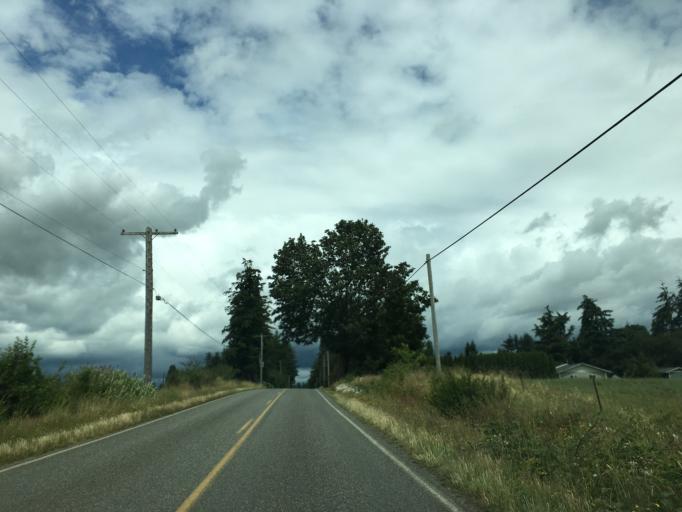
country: US
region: Washington
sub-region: Whatcom County
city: Lynden
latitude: 48.9268
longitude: -122.5300
